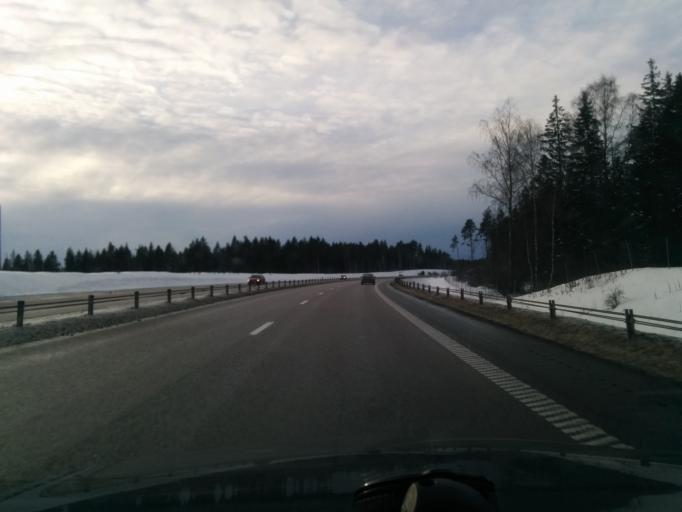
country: SE
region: Uppsala
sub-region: Enkopings Kommun
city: Enkoping
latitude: 59.6440
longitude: 17.0475
